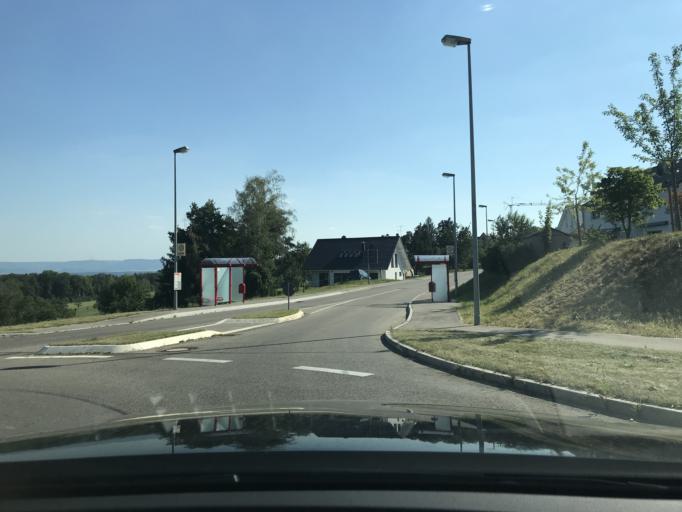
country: DE
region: Baden-Wuerttemberg
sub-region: Regierungsbezirk Stuttgart
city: Baltmannsweiler
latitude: 48.7542
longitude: 9.4859
